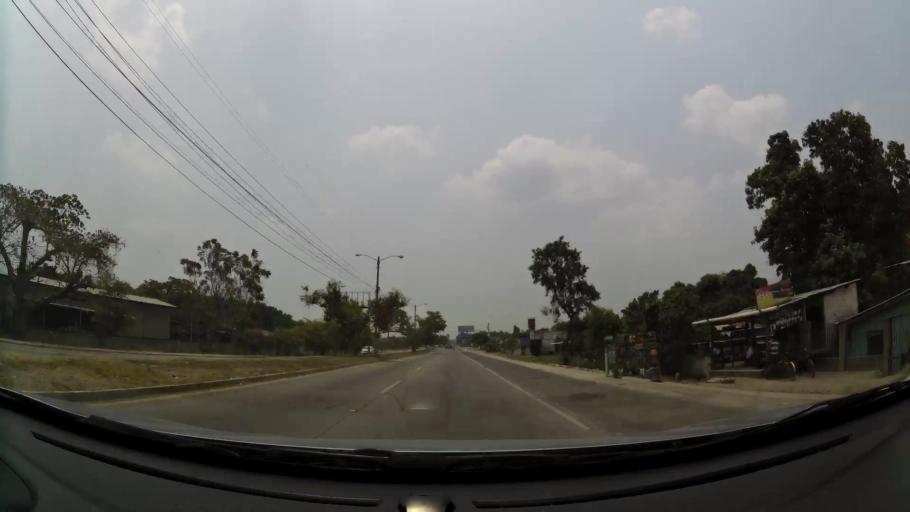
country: HN
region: Cortes
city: La Lima
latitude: 15.4596
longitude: -87.9558
